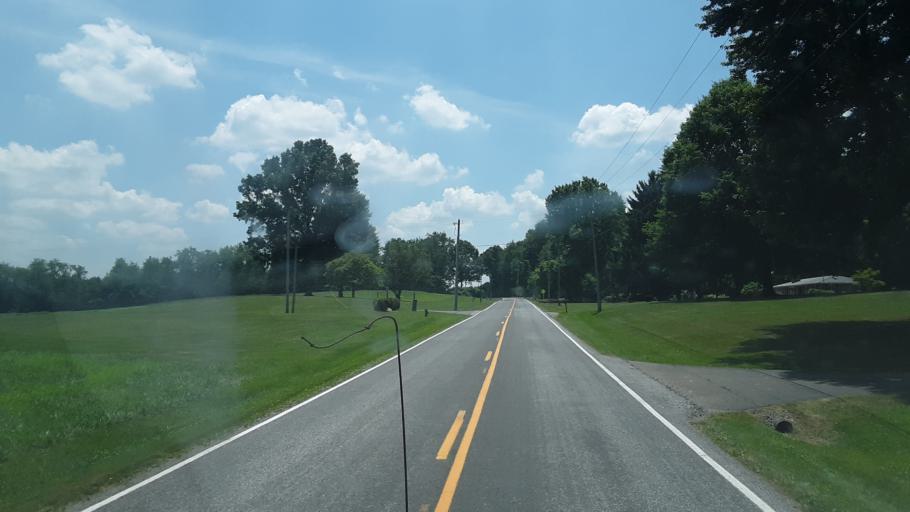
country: US
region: Ohio
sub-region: Stark County
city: Beach City
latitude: 40.6639
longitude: -81.5776
